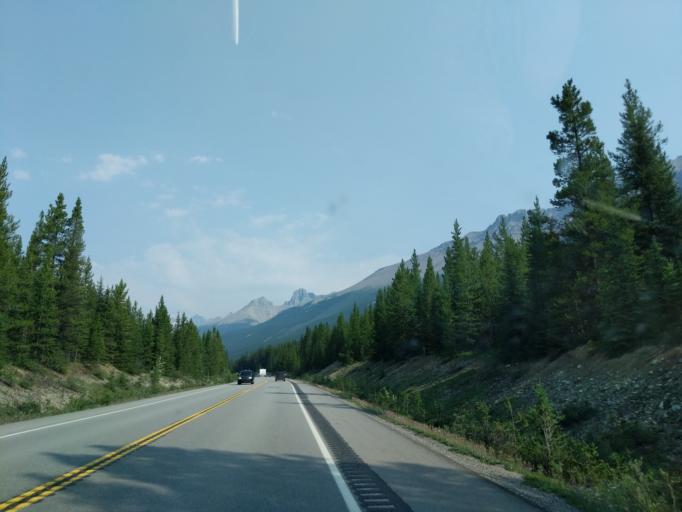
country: CA
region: Alberta
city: Lake Louise
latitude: 51.8018
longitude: -116.5797
